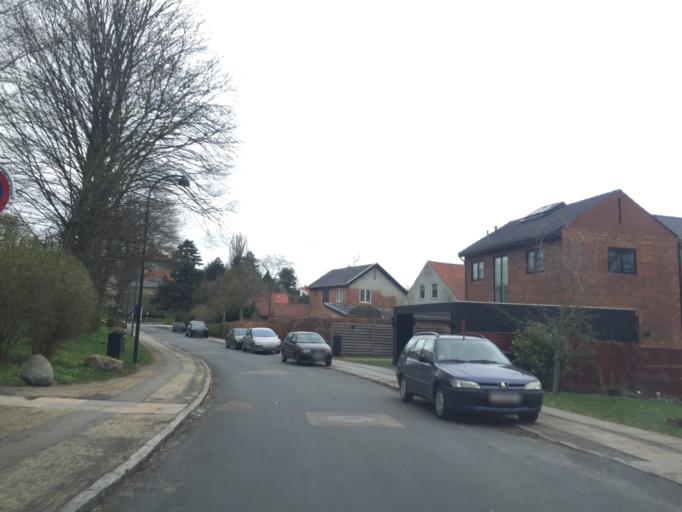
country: DK
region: Capital Region
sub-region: Lyngby-Tarbaek Kommune
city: Kongens Lyngby
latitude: 55.7523
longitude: 12.5260
